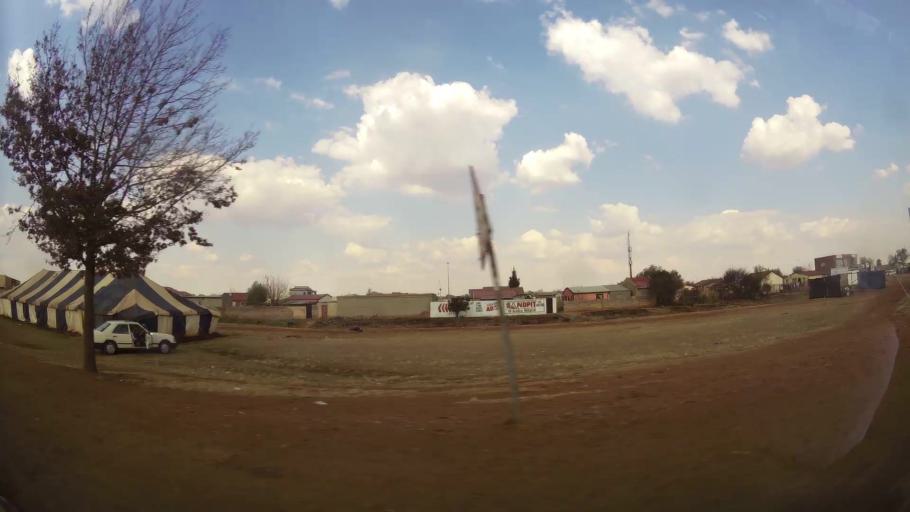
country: ZA
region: Gauteng
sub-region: Ekurhuleni Metropolitan Municipality
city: Germiston
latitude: -26.3145
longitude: 28.1994
